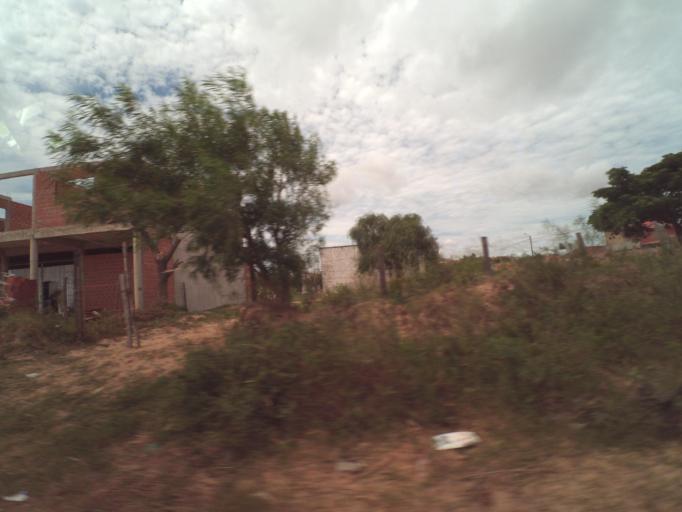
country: BO
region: Santa Cruz
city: Santa Cruz de la Sierra
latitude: -17.8891
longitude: -63.1805
